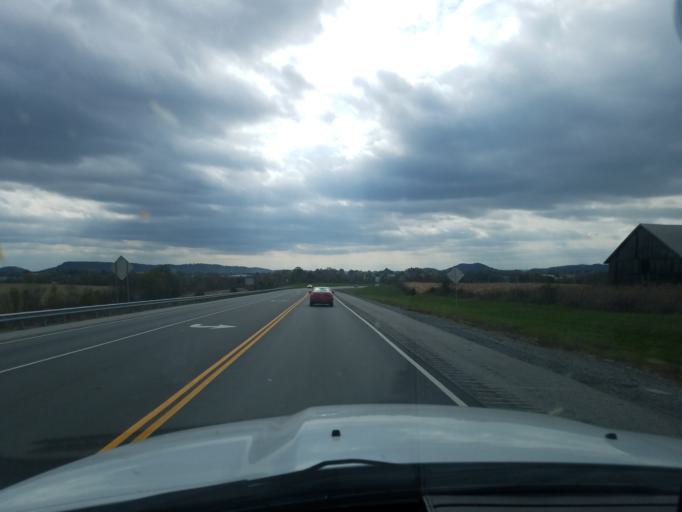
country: US
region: Kentucky
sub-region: Marion County
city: Lebanon
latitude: 37.5710
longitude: -85.2758
